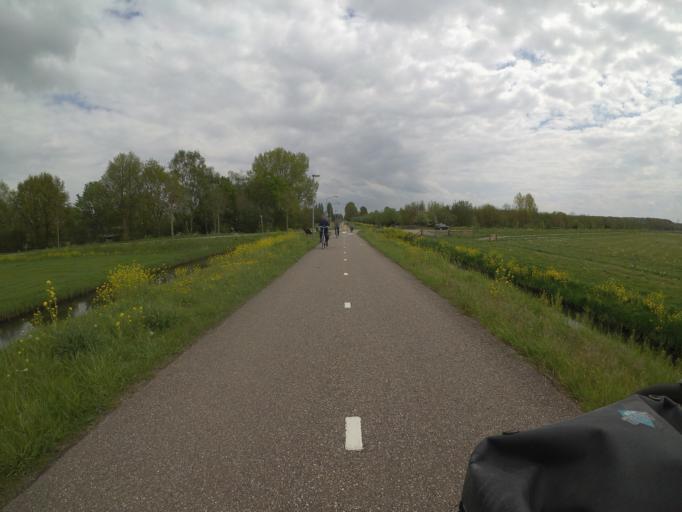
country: NL
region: North Brabant
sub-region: Gemeente Waalwijk
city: Waspik
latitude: 51.6852
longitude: 4.9258
